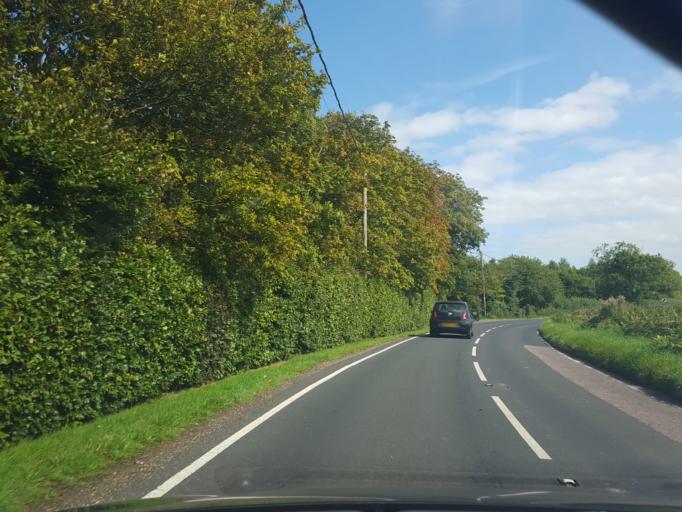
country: GB
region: England
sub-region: Suffolk
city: Shotley Gate
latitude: 51.9366
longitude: 1.1980
